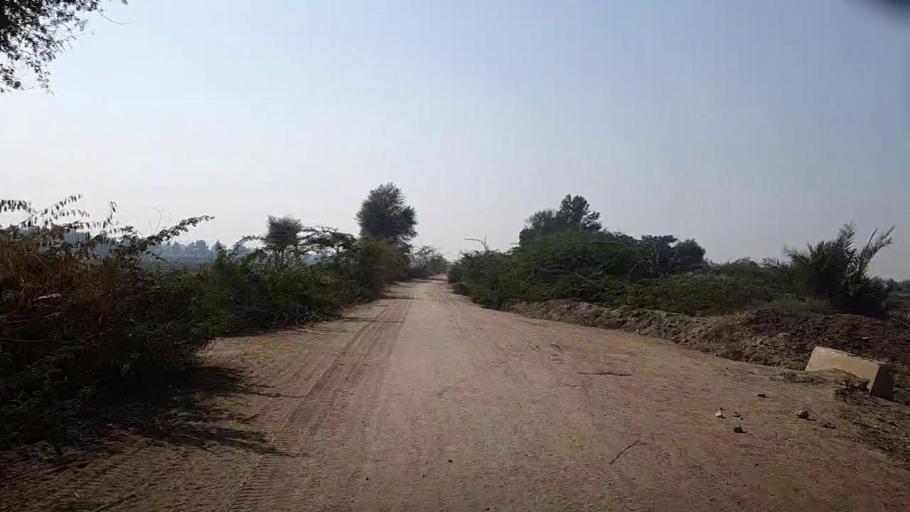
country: PK
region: Sindh
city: Bozdar
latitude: 27.2421
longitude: 68.6027
